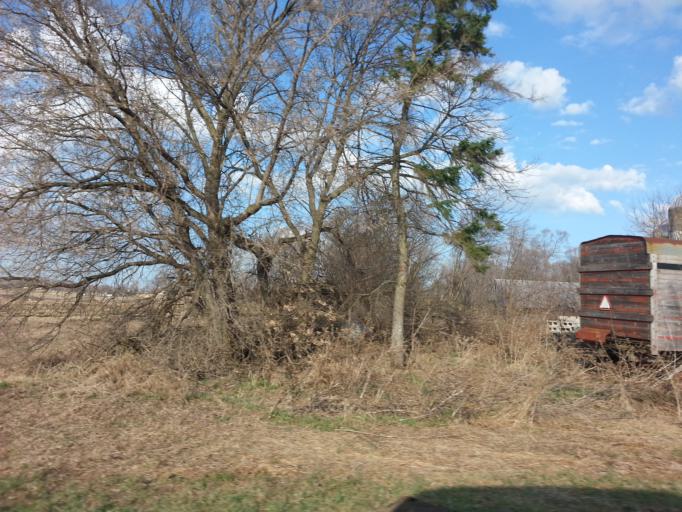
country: US
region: Minnesota
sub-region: Washington County
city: Afton
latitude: 44.8670
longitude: -92.8425
